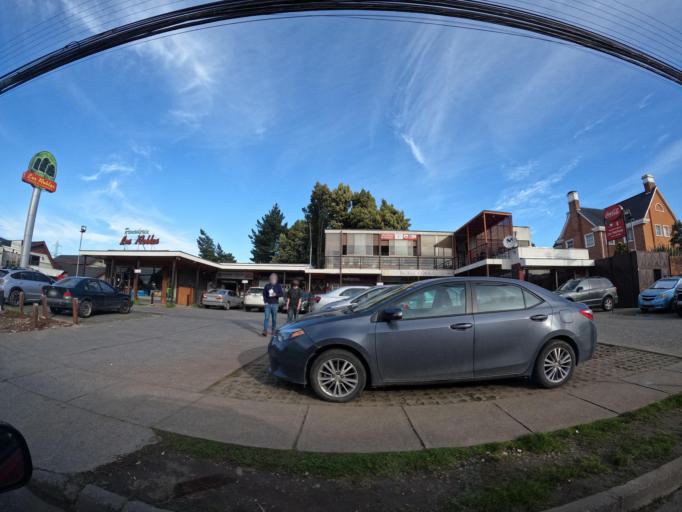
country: CL
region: Biobio
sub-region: Provincia de Concepcion
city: Concepcion
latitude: -36.7890
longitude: -73.0567
